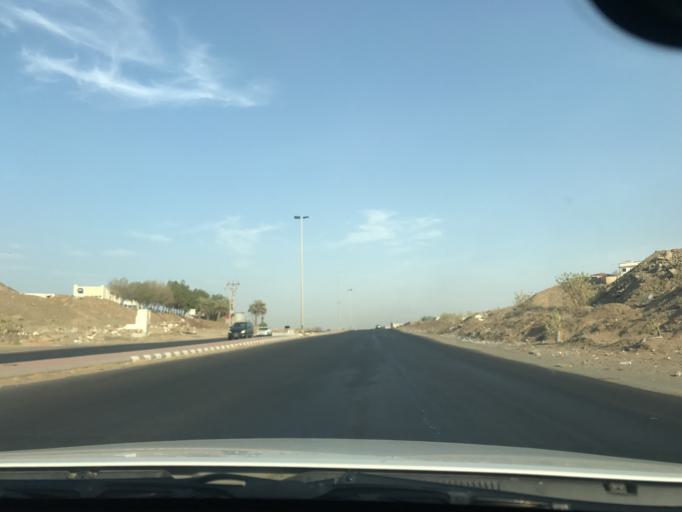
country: SA
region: Makkah
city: Jeddah
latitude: 21.4140
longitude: 39.4169
